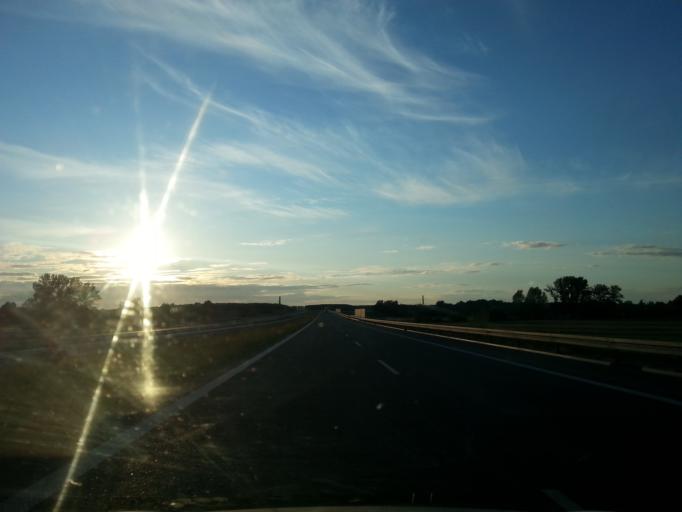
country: PL
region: Lodz Voivodeship
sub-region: Powiat wieruszowski
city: Wieruszow
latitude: 51.3197
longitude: 18.1625
